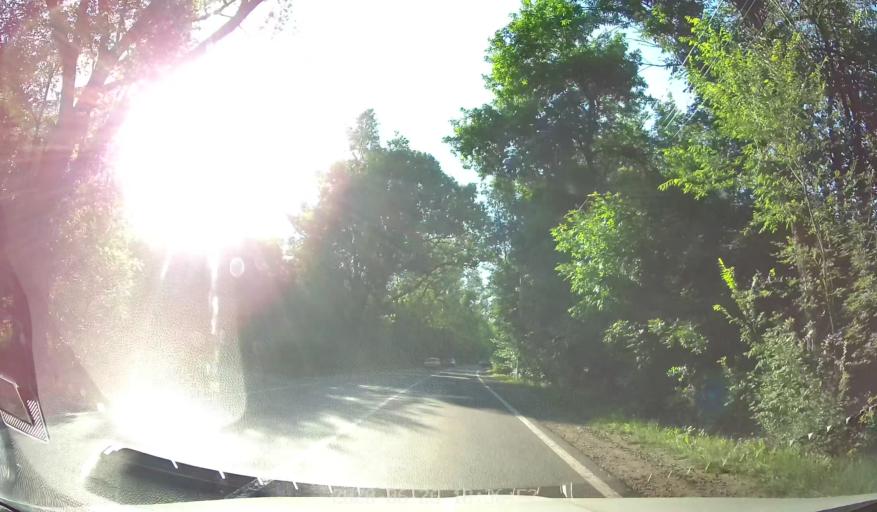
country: MD
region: Chisinau
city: Singera
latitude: 46.9467
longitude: 28.9340
